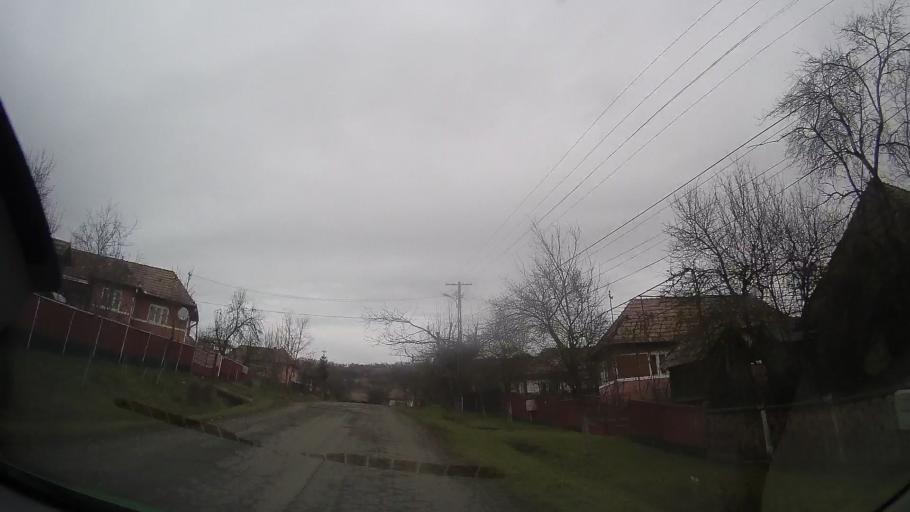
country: RO
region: Mures
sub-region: Comuna Bala
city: Bala
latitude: 46.7106
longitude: 24.5017
